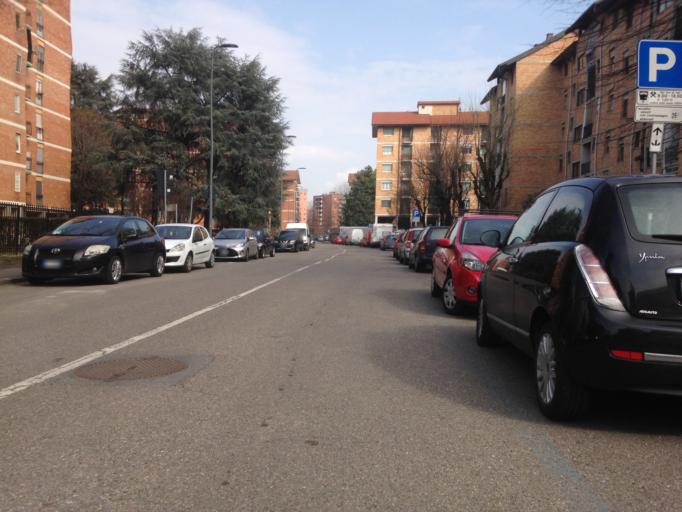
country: IT
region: Lombardy
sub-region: Citta metropolitana di Milano
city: Milano
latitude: 45.4253
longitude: 9.1741
